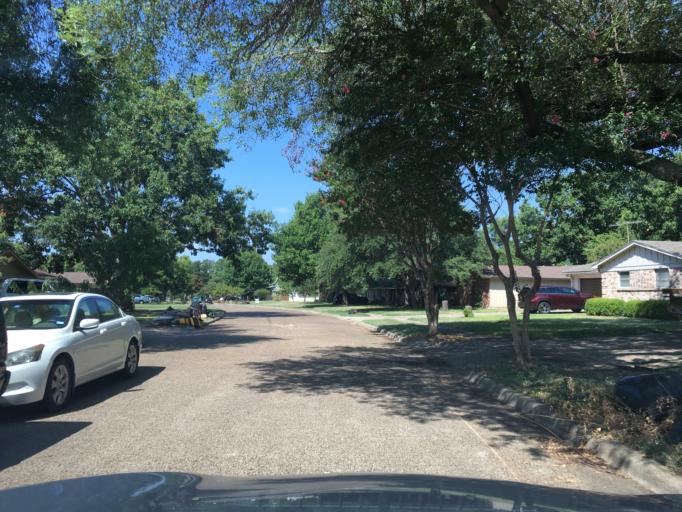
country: US
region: Texas
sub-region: Dallas County
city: Garland
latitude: 32.8618
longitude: -96.6838
